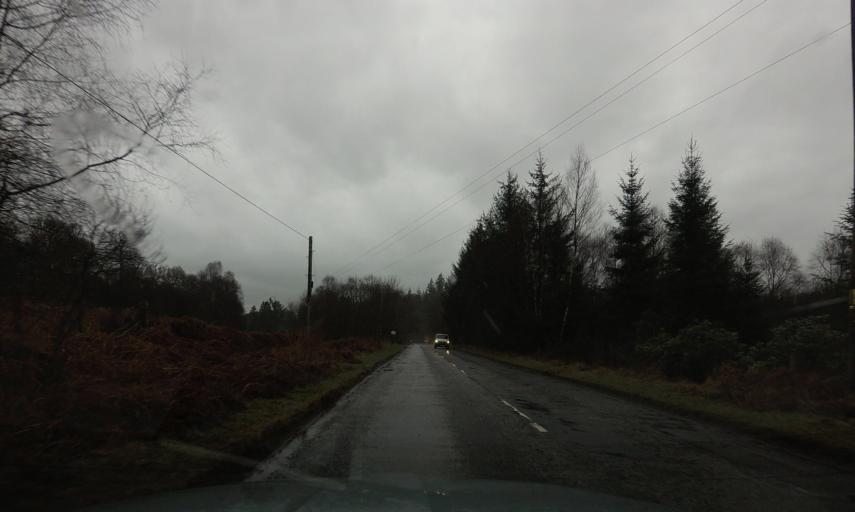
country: GB
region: Scotland
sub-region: Stirling
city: Balfron
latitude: 56.1596
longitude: -4.3631
